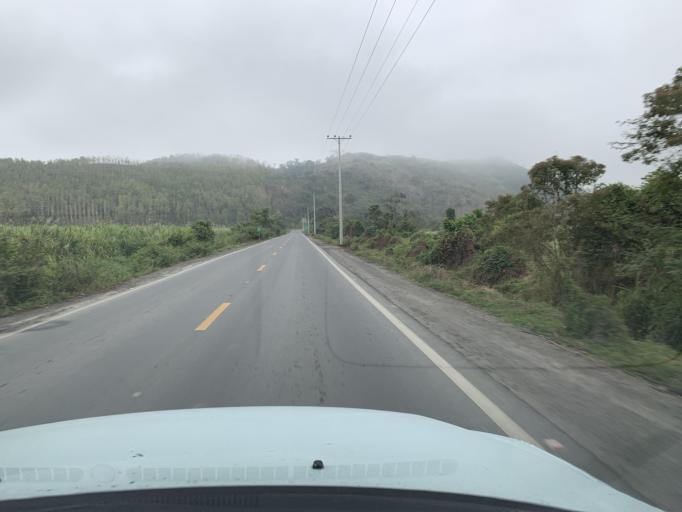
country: EC
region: Guayas
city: Coronel Marcelino Mariduena
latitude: -2.3501
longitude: -79.5294
